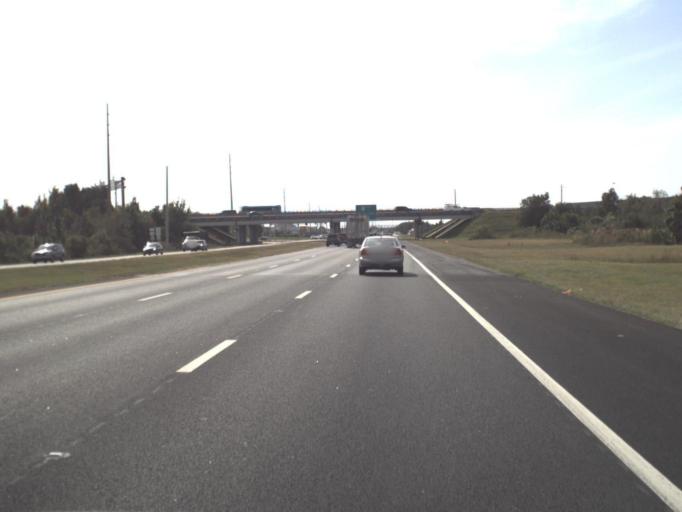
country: US
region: Florida
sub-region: Orange County
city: Williamsburg
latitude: 28.4246
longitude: -81.4230
